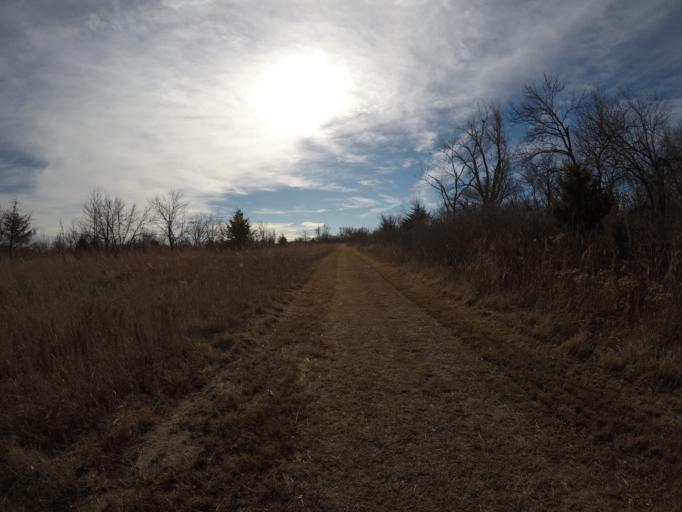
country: US
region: Kansas
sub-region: Reno County
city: Buhler
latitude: 38.1244
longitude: -97.8568
